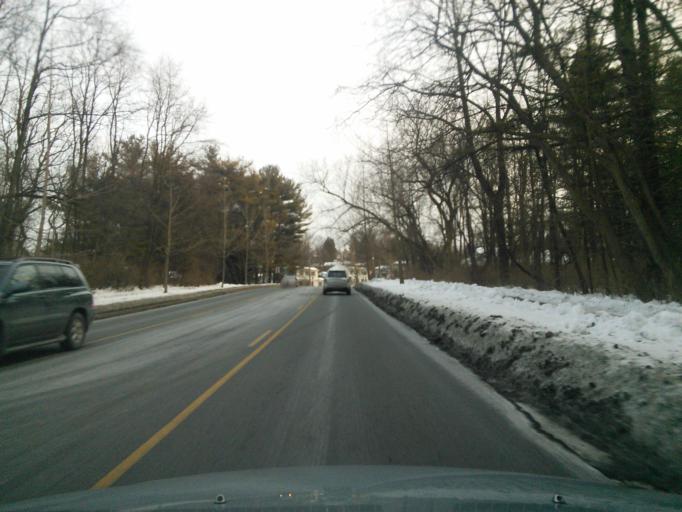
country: US
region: Pennsylvania
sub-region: Centre County
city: State College
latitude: 40.7948
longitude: -77.8413
